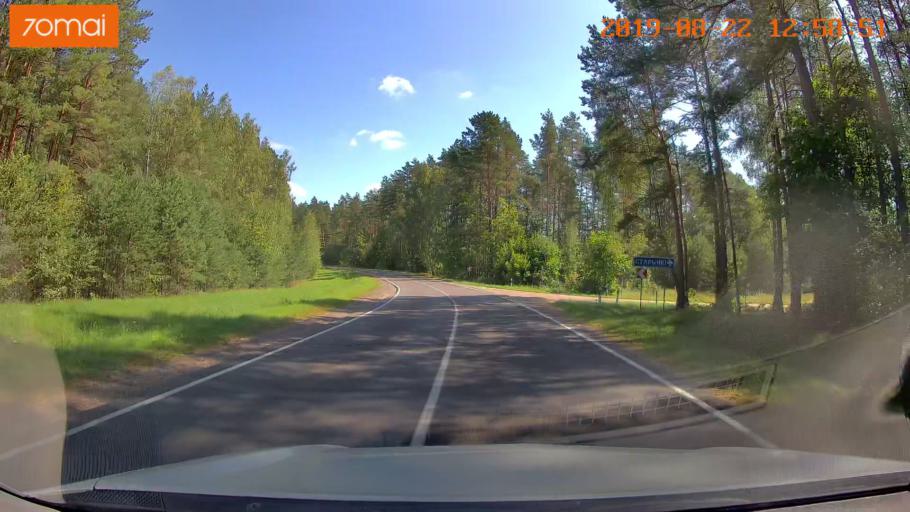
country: BY
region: Minsk
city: Prawdzinski
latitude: 53.4219
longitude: 27.7802
